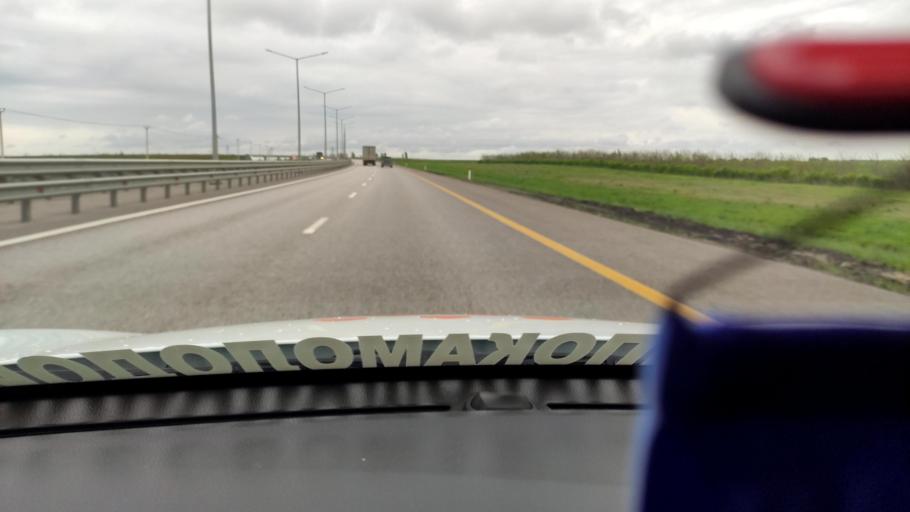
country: RU
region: Voronezj
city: Novaya Usman'
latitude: 51.5940
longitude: 39.3619
